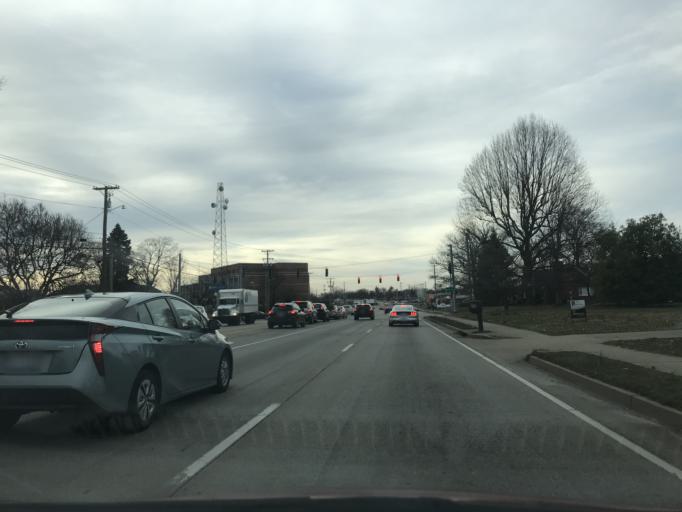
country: US
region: Kentucky
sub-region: Jefferson County
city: West Buechel
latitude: 38.1984
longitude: -85.6827
